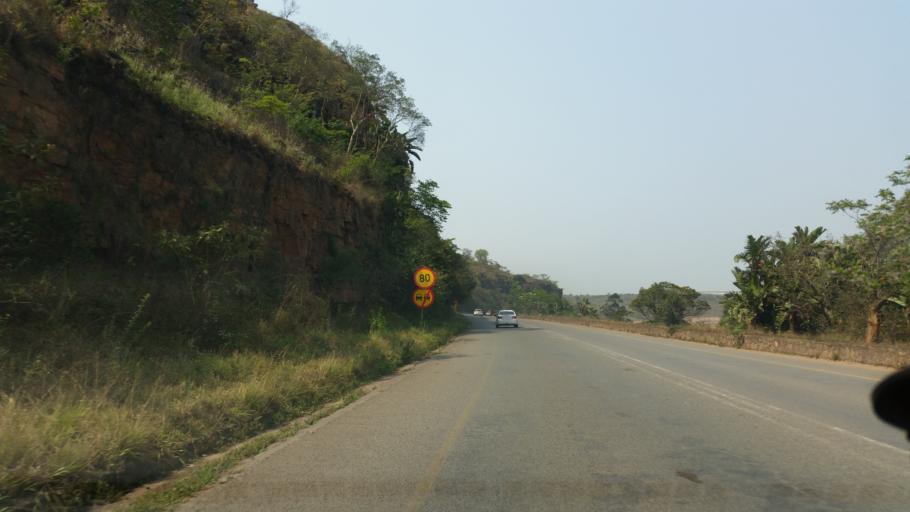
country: ZA
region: KwaZulu-Natal
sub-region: eThekwini Metropolitan Municipality
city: Mpumalanga
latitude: -29.7486
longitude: 30.6647
